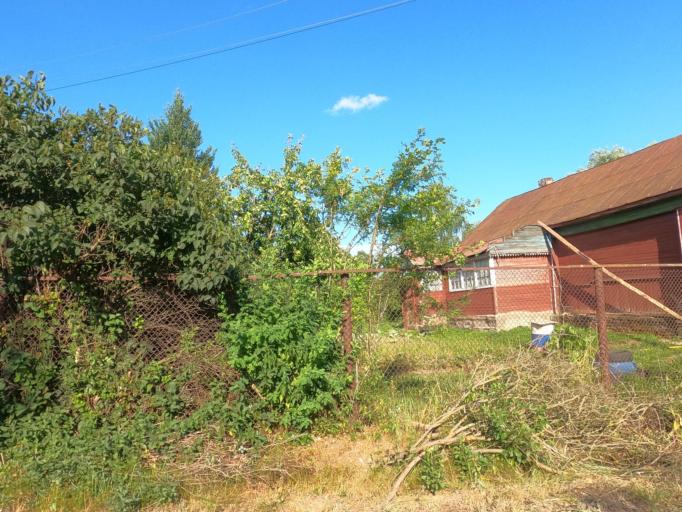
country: RU
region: Moskovskaya
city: Konobeyevo
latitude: 55.4137
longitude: 38.6944
